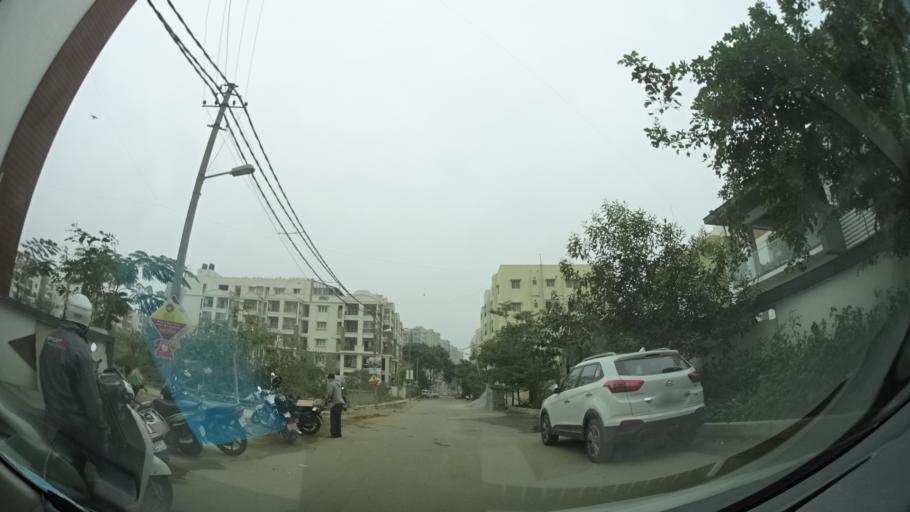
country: IN
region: Karnataka
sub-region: Bangalore Rural
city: Hoskote
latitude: 12.9673
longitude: 77.7398
